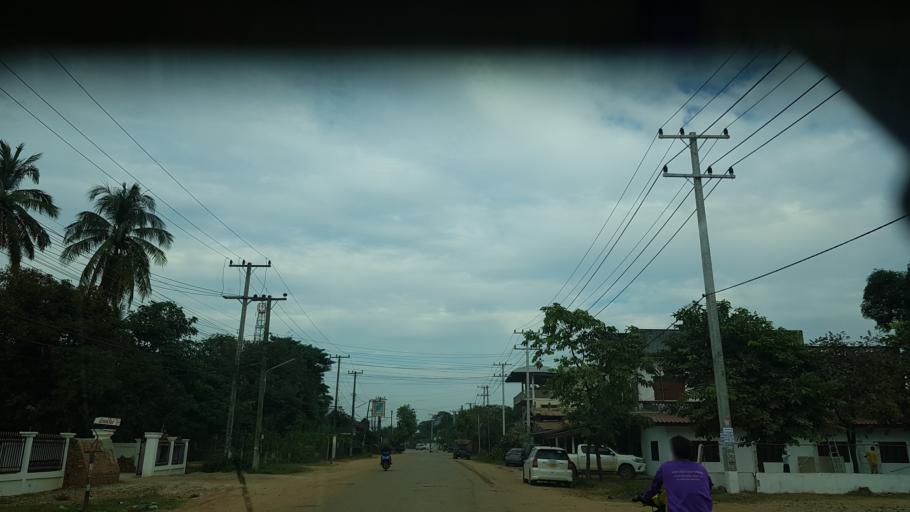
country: TH
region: Nong Khai
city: Nong Khai
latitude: 17.8890
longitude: 102.7392
